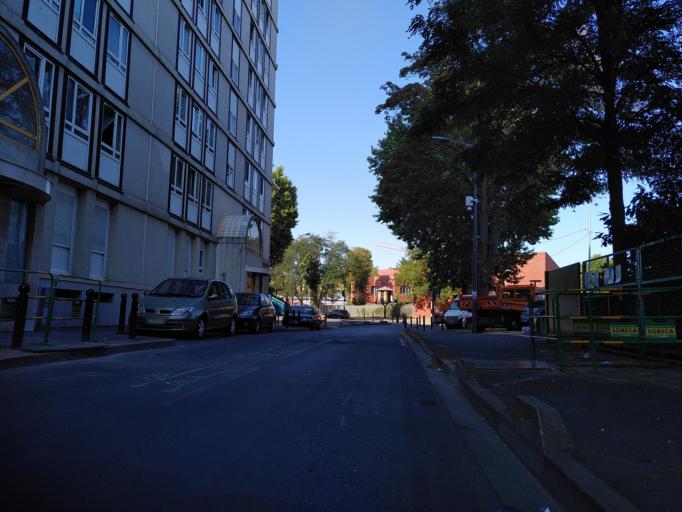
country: FR
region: Ile-de-France
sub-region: Departement du Val-de-Marne
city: Villeneuve-le-Roi
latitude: 48.7472
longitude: 2.4122
